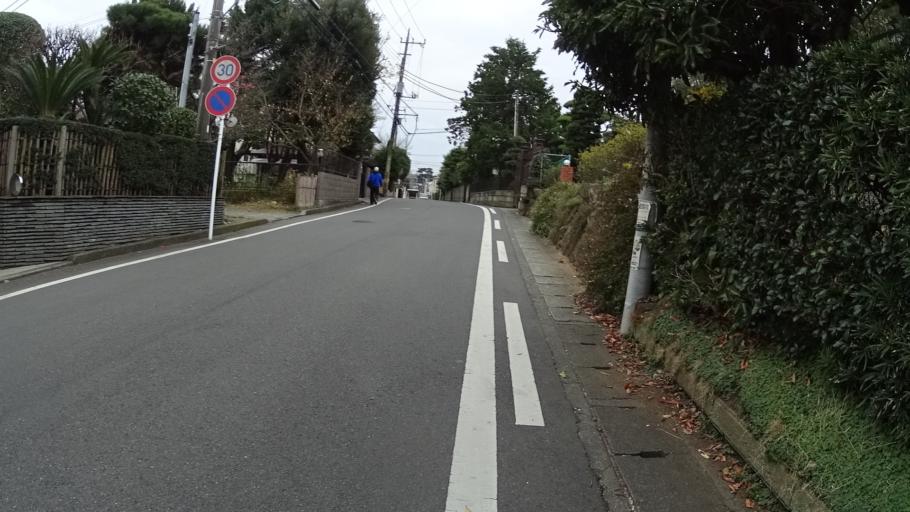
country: JP
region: Kanagawa
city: Oiso
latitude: 35.3106
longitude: 139.3082
